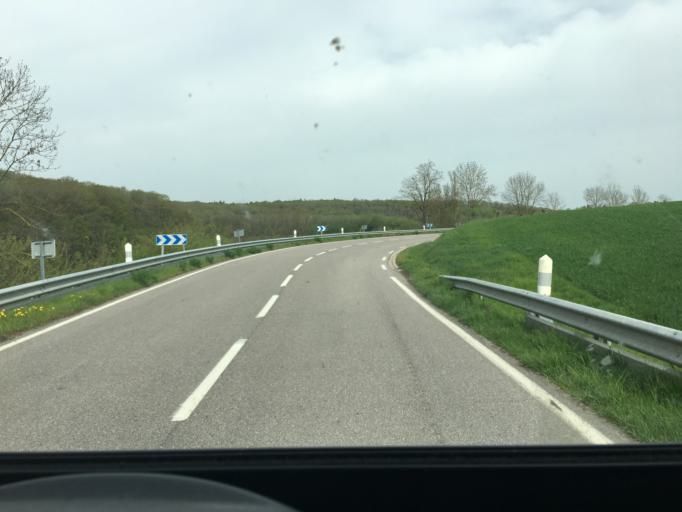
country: FR
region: Lorraine
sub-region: Departement de la Moselle
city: Vic-sur-Seille
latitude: 48.7458
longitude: 6.5400
